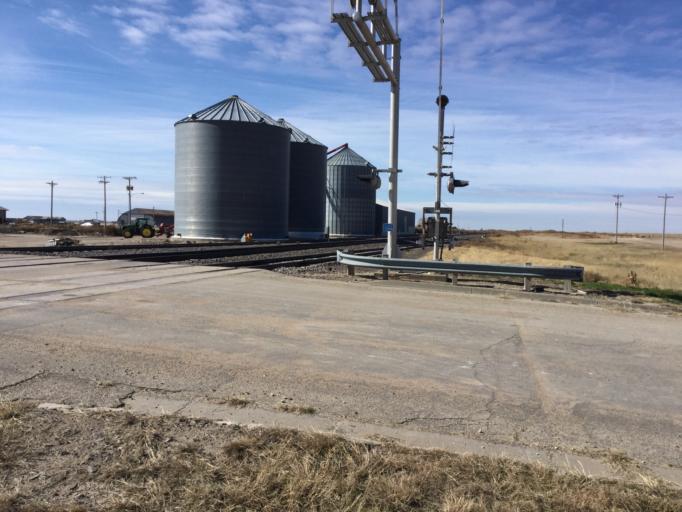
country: US
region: Kansas
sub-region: Trego County
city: WaKeeney
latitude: 39.0238
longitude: -99.8901
